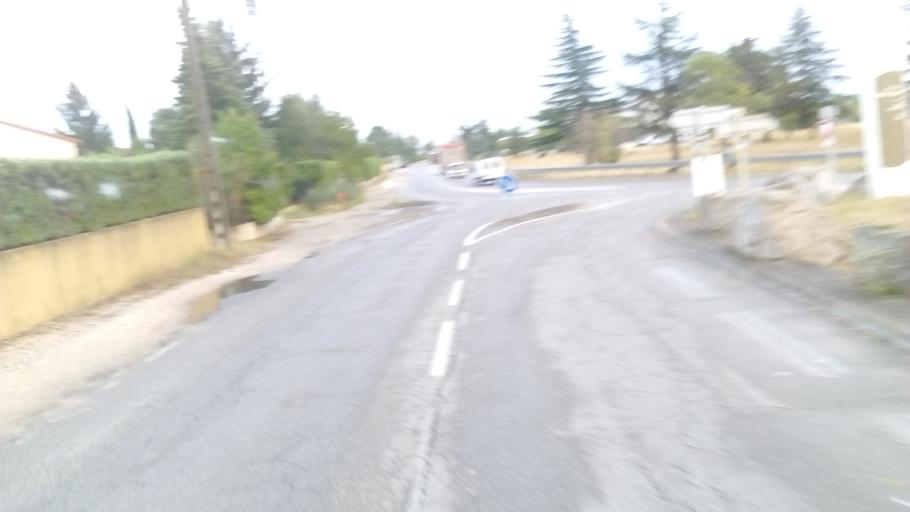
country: FR
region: Rhone-Alpes
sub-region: Departement de l'Ardeche
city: Cornas
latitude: 44.9628
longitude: 4.8758
